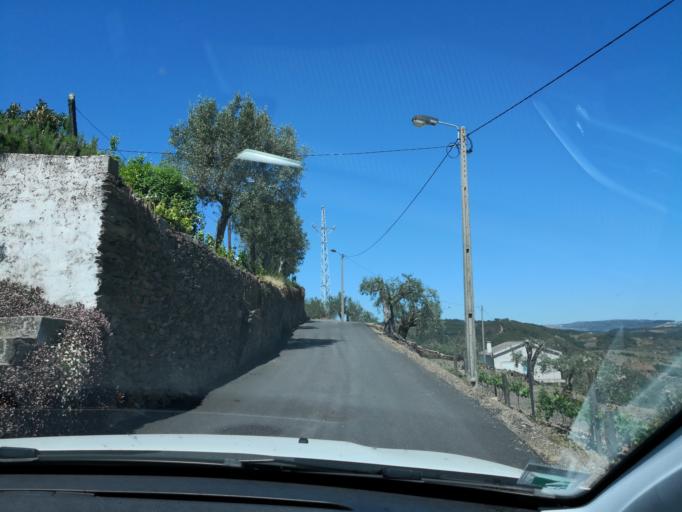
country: PT
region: Vila Real
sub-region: Vila Real
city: Vila Real
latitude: 41.2308
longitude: -7.7291
